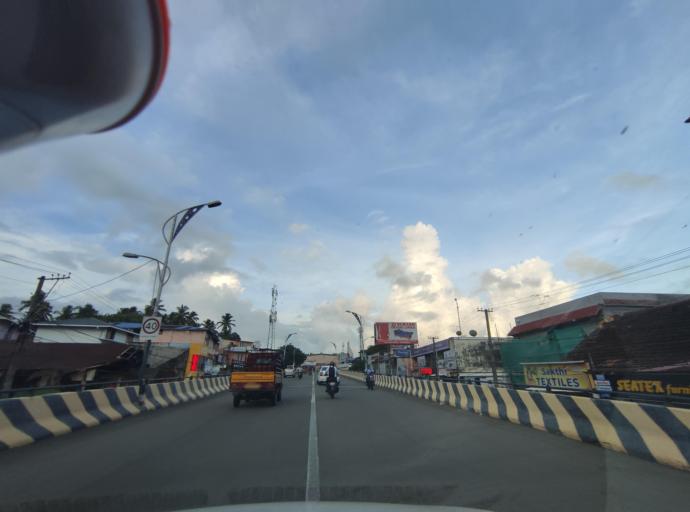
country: IN
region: Kerala
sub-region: Thiruvananthapuram
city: Thiruvananthapuram
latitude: 8.4864
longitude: 76.9457
